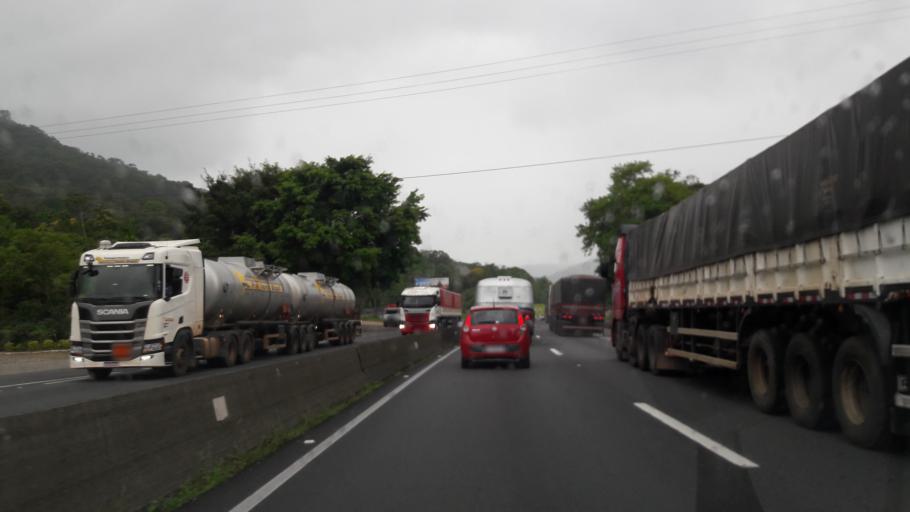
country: BR
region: Parana
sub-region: Antonina
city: Antonina
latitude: -25.5735
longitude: -48.8259
